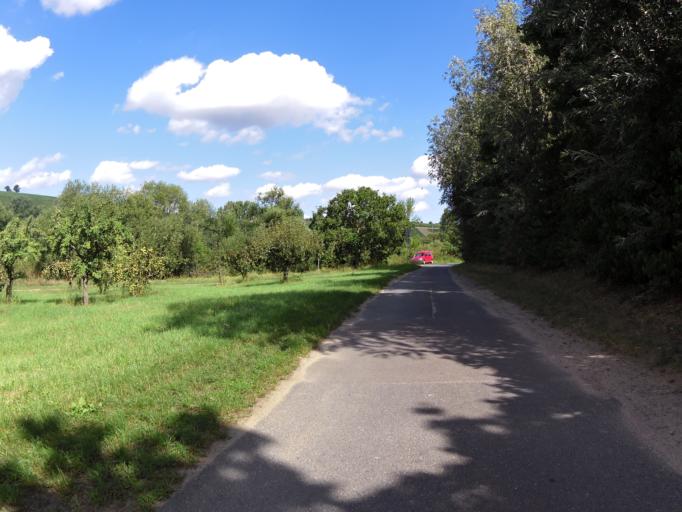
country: DE
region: Bavaria
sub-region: Regierungsbezirk Unterfranken
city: Nordheim
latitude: 49.8543
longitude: 10.1742
